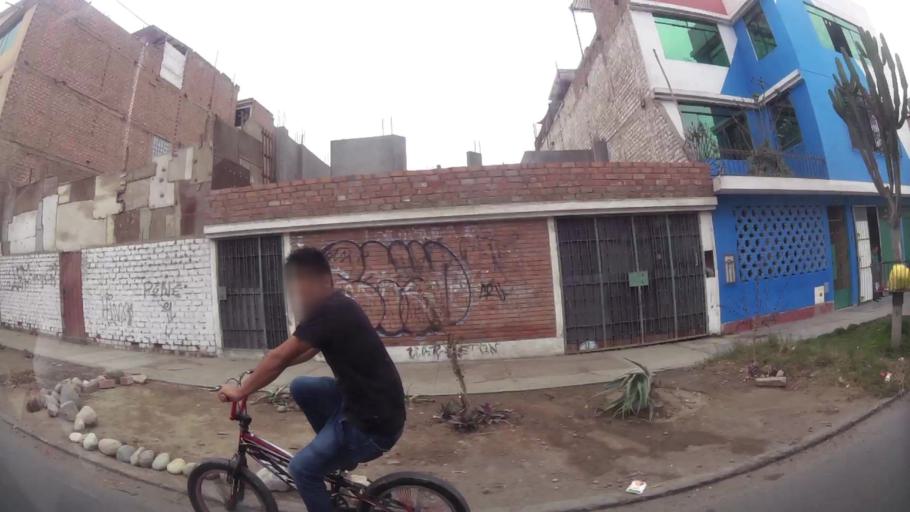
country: PE
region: Lima
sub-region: Lima
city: Independencia
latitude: -11.9340
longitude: -77.0811
